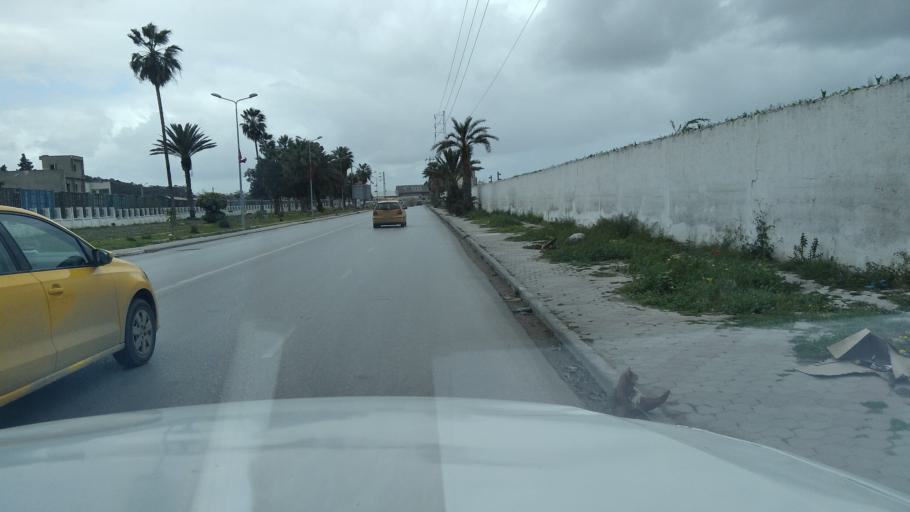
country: TN
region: Bin 'Arus
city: Ben Arous
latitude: 36.7578
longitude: 10.2183
